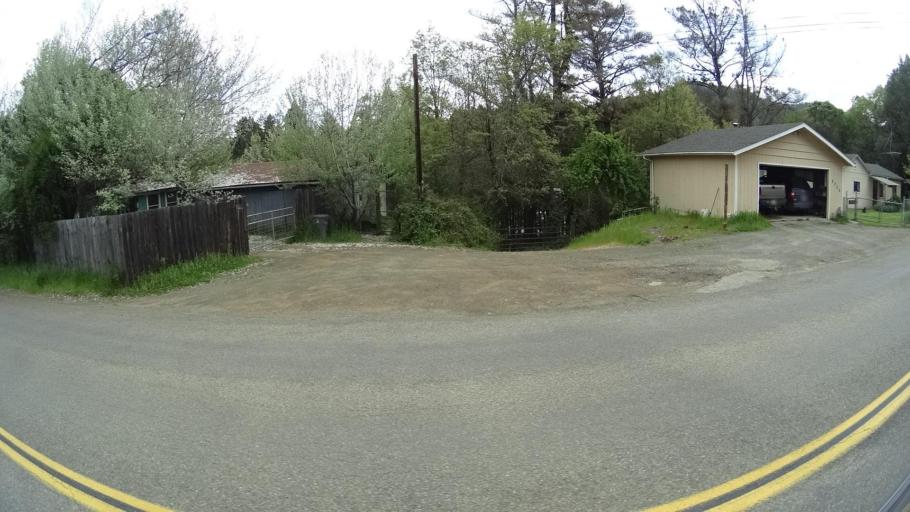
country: US
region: California
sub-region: Humboldt County
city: Redway
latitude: 40.1068
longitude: -123.9035
